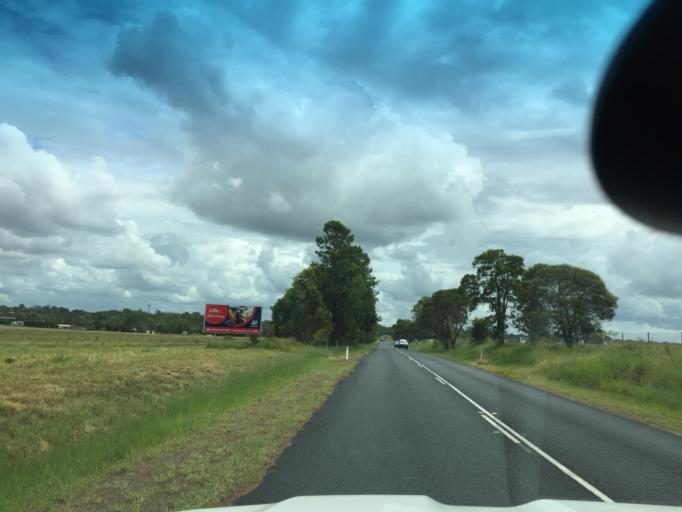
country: AU
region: Queensland
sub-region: Moreton Bay
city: Morayfield
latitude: -27.1145
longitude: 152.9798
